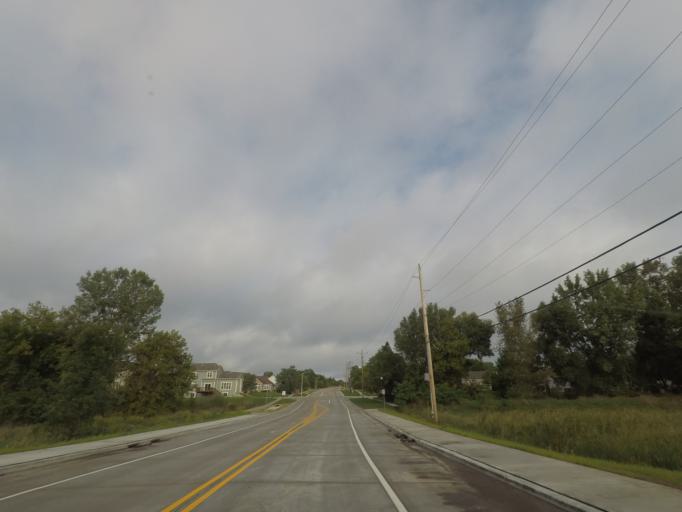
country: US
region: Wisconsin
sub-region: Waukesha County
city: Waukesha
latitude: 43.0326
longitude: -88.2772
